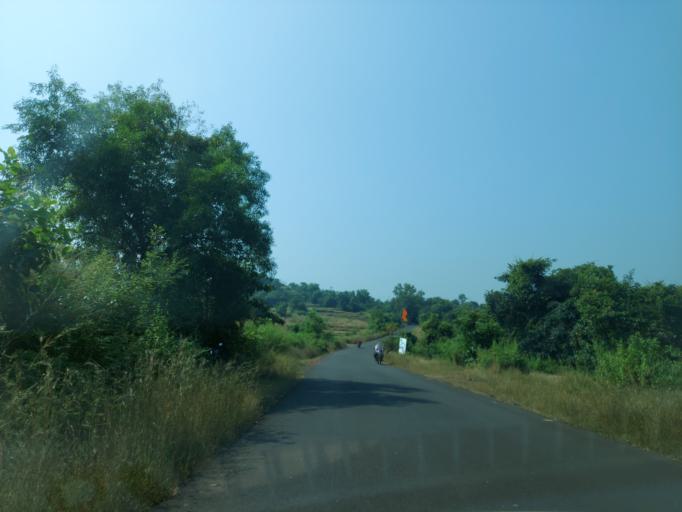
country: IN
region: Maharashtra
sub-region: Sindhudurg
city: Kudal
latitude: 15.9757
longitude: 73.6508
